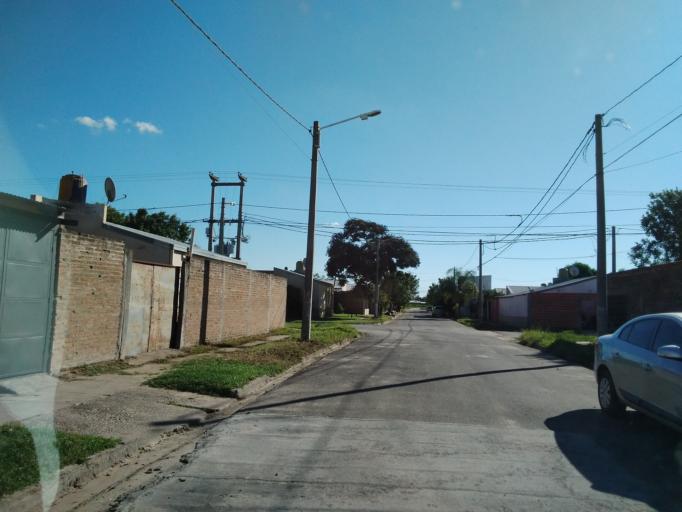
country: AR
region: Corrientes
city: Corrientes
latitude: -27.4573
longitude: -58.7683
